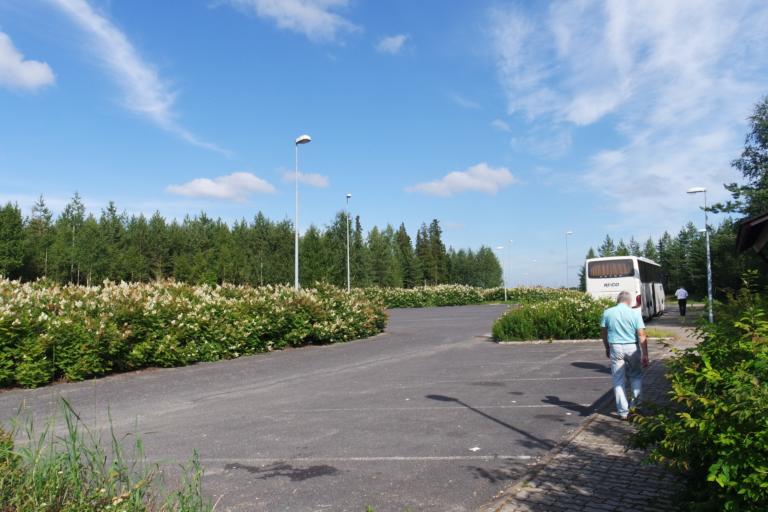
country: FI
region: Lapland
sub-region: Kemi-Tornio
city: Keminmaa
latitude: 65.8247
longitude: 24.4105
